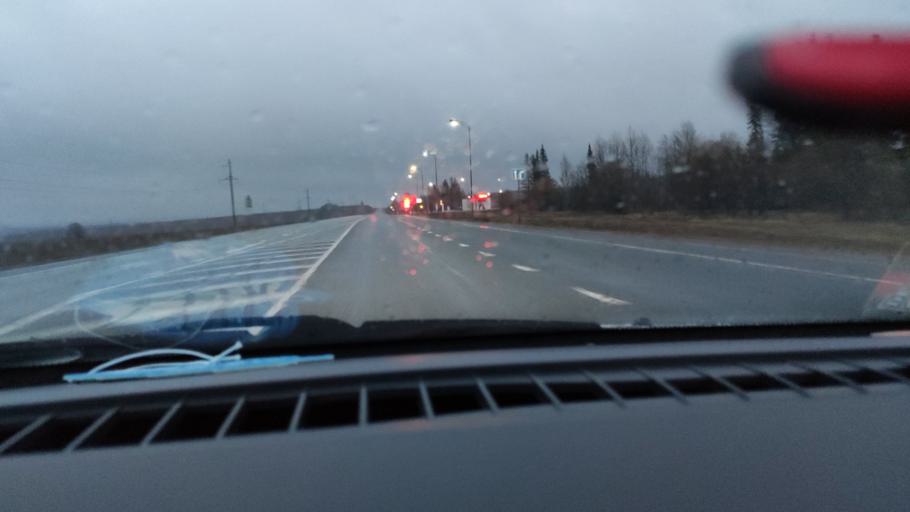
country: RU
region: Udmurtiya
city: Alnashi
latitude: 56.2512
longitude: 52.3830
